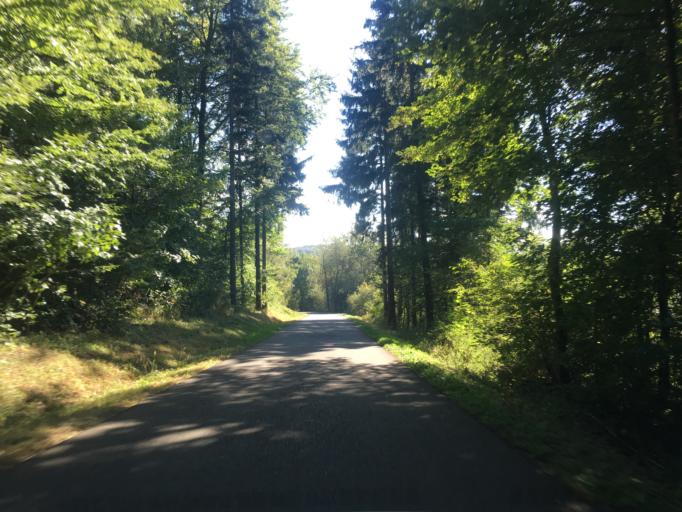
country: DE
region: Baden-Wuerttemberg
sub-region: Tuebingen Region
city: Pfullingen
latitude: 48.4124
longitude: 9.2154
